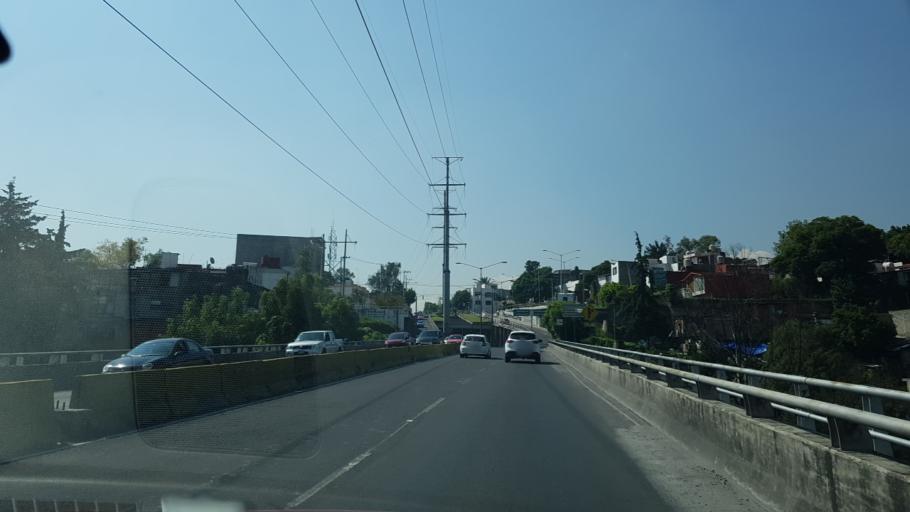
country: MX
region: Mexico City
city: Alvaro Obregon
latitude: 19.3618
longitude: -99.2061
